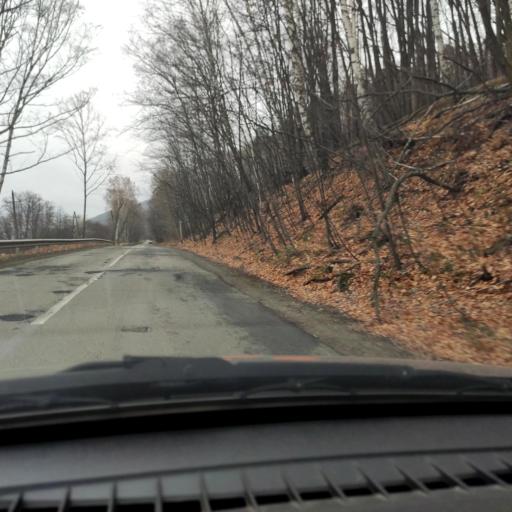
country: RU
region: Samara
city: Pribrezhnyy
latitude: 53.4383
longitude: 49.7099
